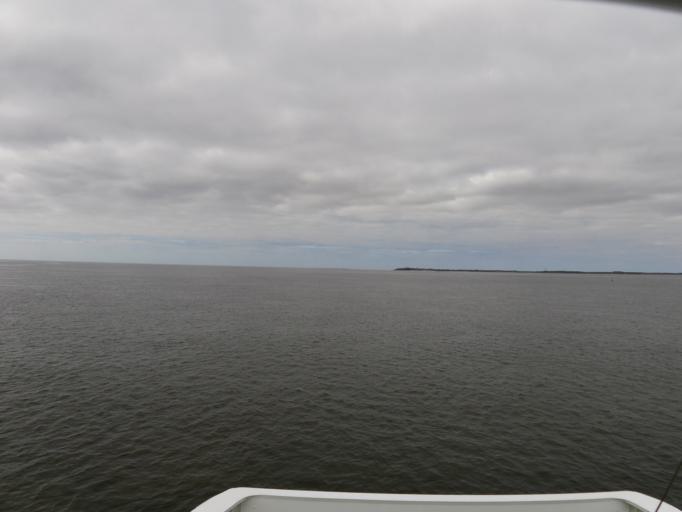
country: DE
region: Schleswig-Holstein
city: Borgsum
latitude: 54.6435
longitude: 8.4546
